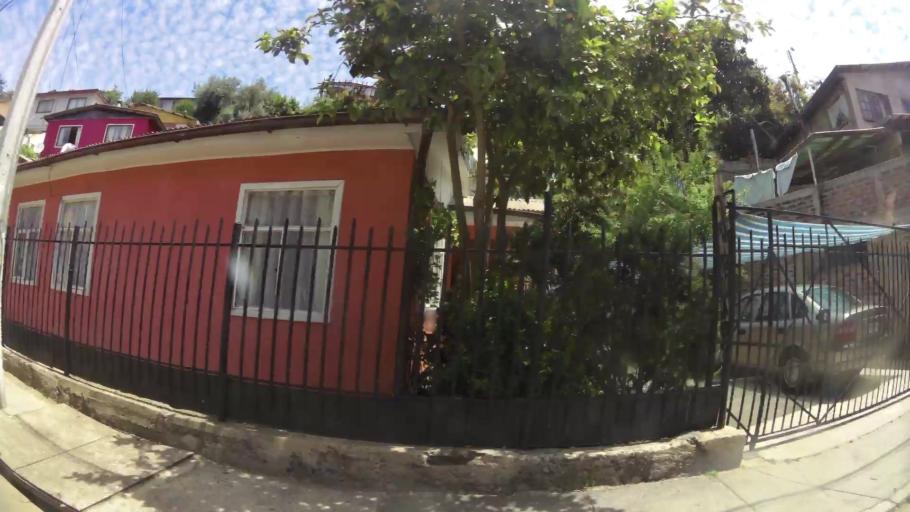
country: CL
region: Valparaiso
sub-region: Provincia de Valparaiso
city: Vina del Mar
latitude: -33.0508
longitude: -71.5719
